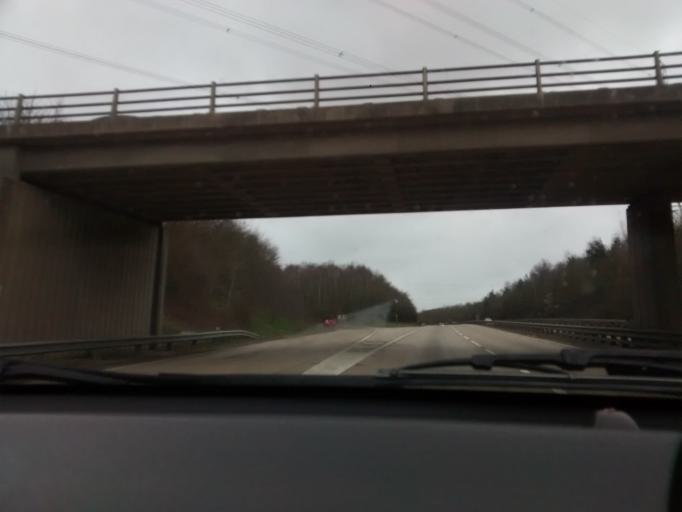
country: GB
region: England
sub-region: Suffolk
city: Bramford
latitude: 52.0864
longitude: 1.1125
